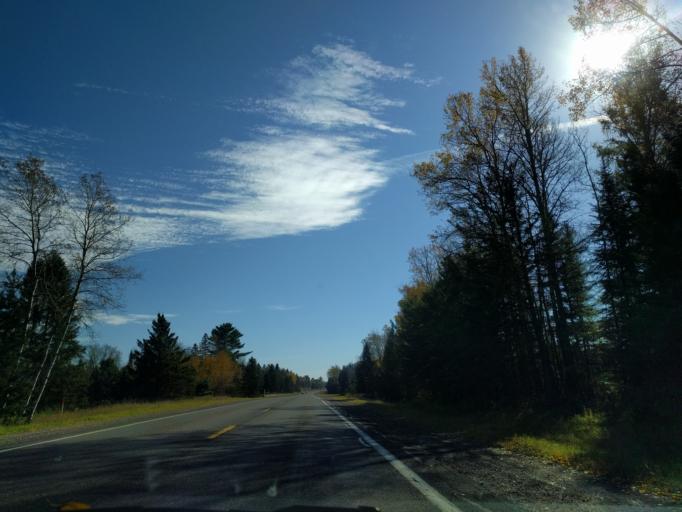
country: US
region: Michigan
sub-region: Marquette County
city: West Ishpeming
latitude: 46.3365
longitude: -87.9729
